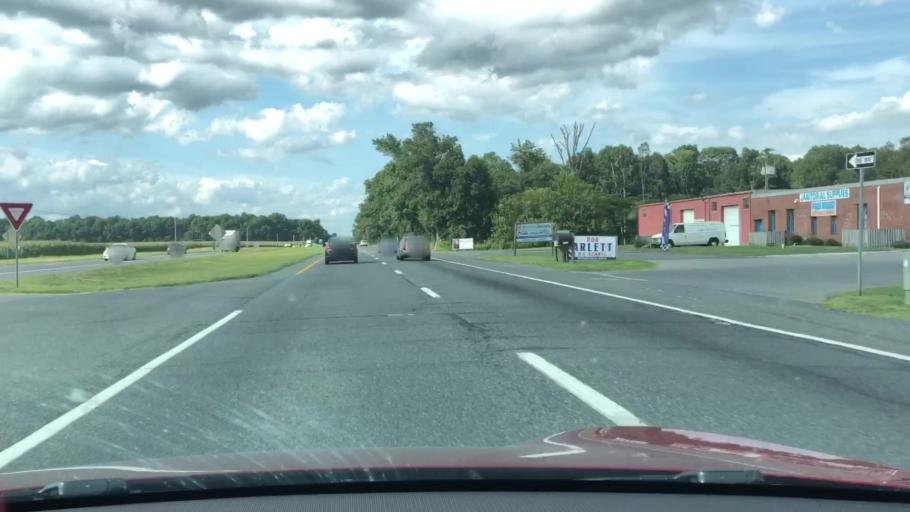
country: US
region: Delaware
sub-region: Sussex County
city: Bridgeville
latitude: 38.7622
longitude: -75.5932
